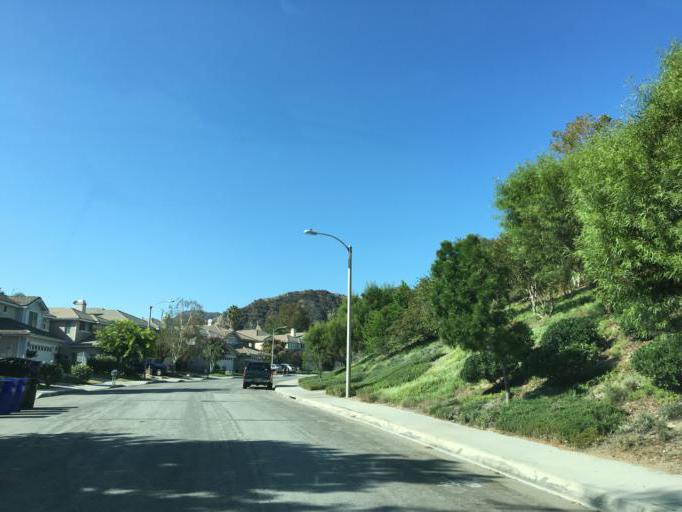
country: US
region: California
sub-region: Los Angeles County
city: Santa Clarita
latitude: 34.3863
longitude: -118.5890
